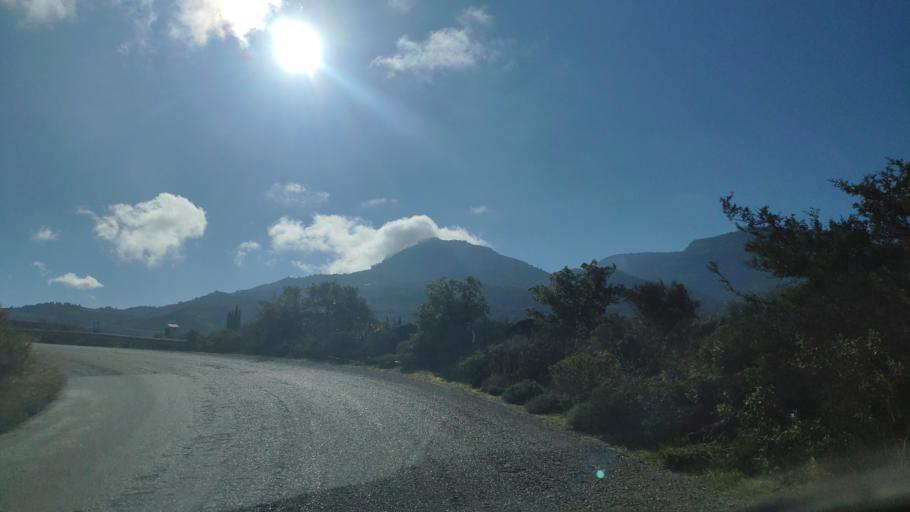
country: GR
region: West Greece
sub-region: Nomos Achaias
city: Aiyira
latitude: 38.0968
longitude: 22.4386
